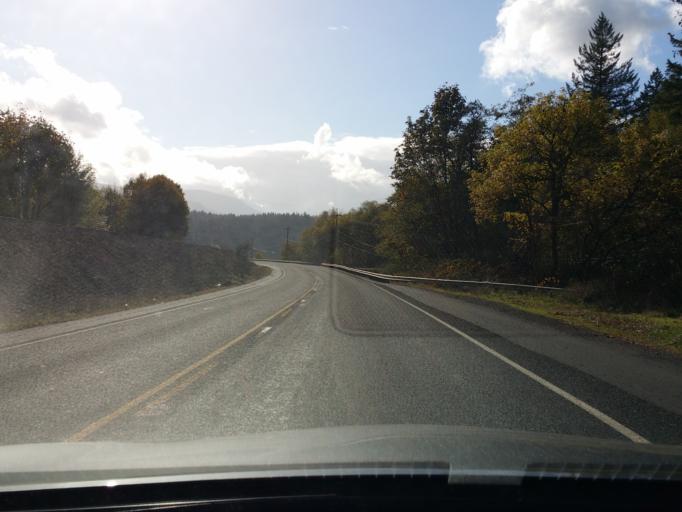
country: US
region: Oregon
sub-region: Hood River County
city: Cascade Locks
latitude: 45.6796
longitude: -121.9059
